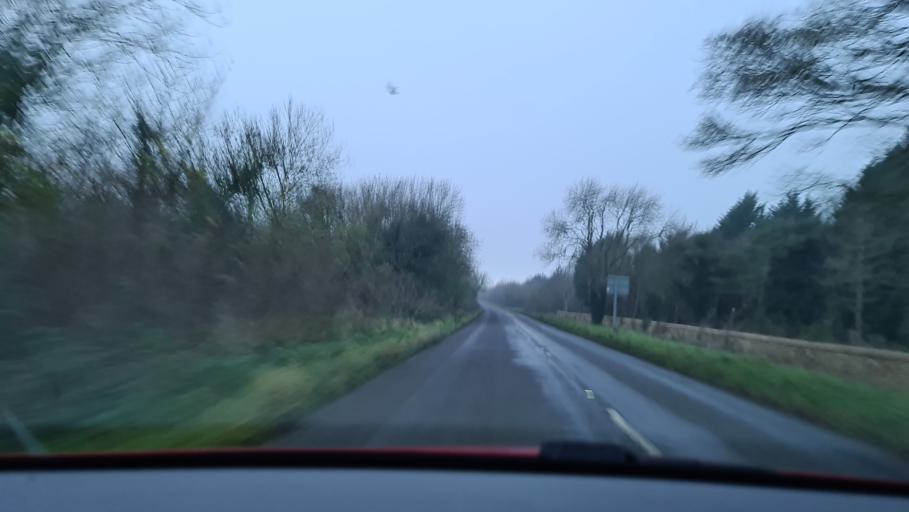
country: GB
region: England
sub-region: Oxfordshire
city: Bicester
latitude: 51.8916
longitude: -1.1994
